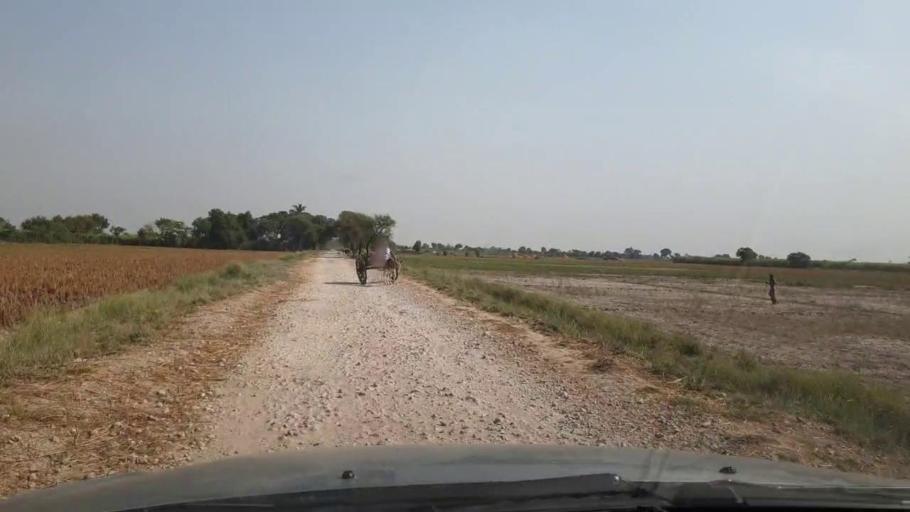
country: PK
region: Sindh
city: Bulri
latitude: 24.9101
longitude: 68.3697
